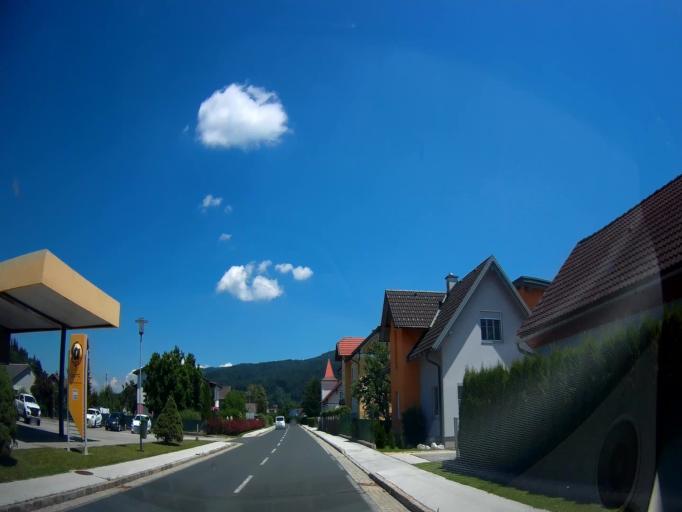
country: AT
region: Carinthia
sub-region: Politischer Bezirk Volkermarkt
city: Bleiburg/Pliberk
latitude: 46.5787
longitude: 14.7921
